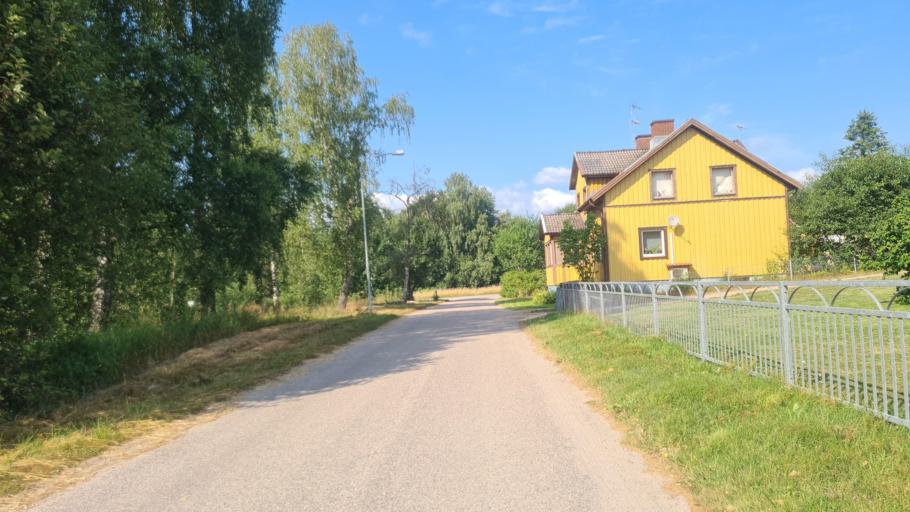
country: SE
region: Kronoberg
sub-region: Ljungby Kommun
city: Ljungby
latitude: 56.7397
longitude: 13.8756
